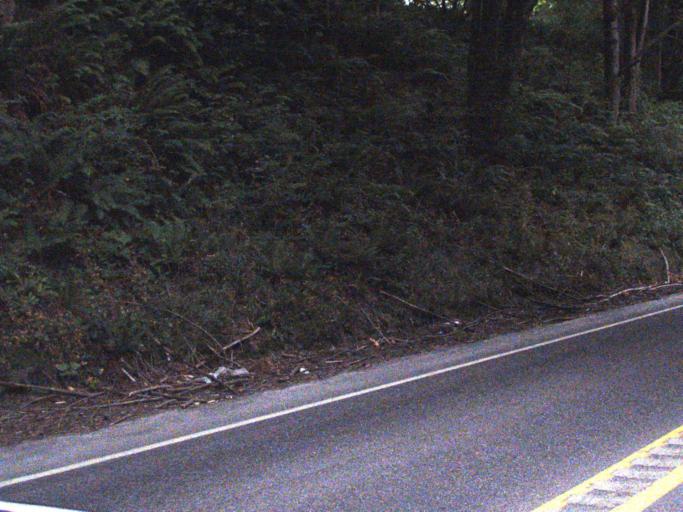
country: US
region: Washington
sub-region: King County
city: Fall City
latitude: 47.5658
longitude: -121.8702
